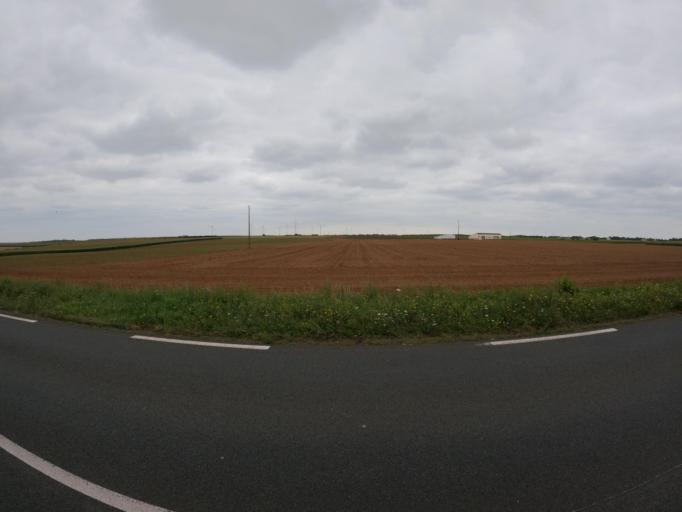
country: FR
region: Pays de la Loire
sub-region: Departement de la Vendee
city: Serigne
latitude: 46.4821
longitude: -0.8845
